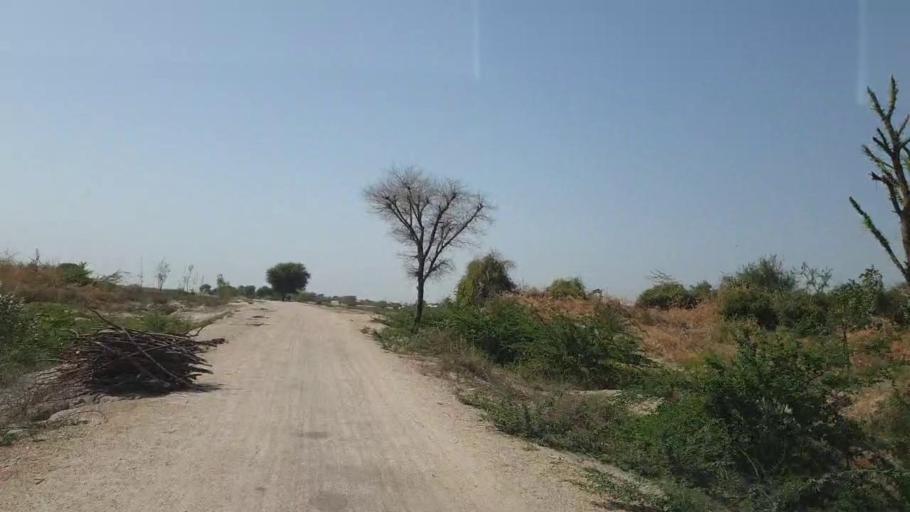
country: PK
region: Sindh
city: Naukot
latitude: 24.9104
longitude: 69.5111
